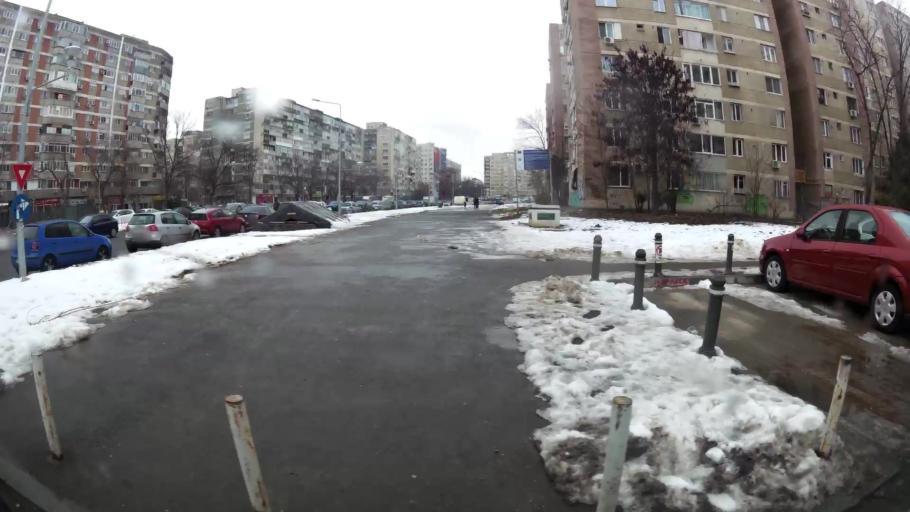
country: RO
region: Ilfov
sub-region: Comuna Chiajna
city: Rosu
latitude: 44.4184
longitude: 26.0207
